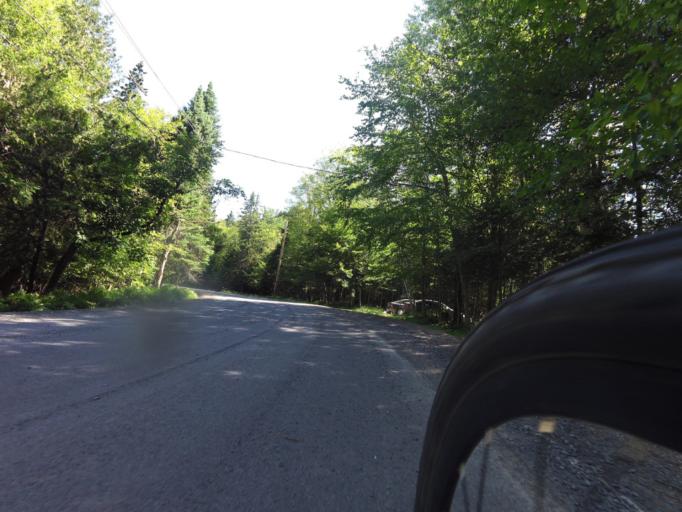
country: CA
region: Quebec
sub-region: Laurentides
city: Brownsburg-Chatham
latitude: 45.8349
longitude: -74.5450
